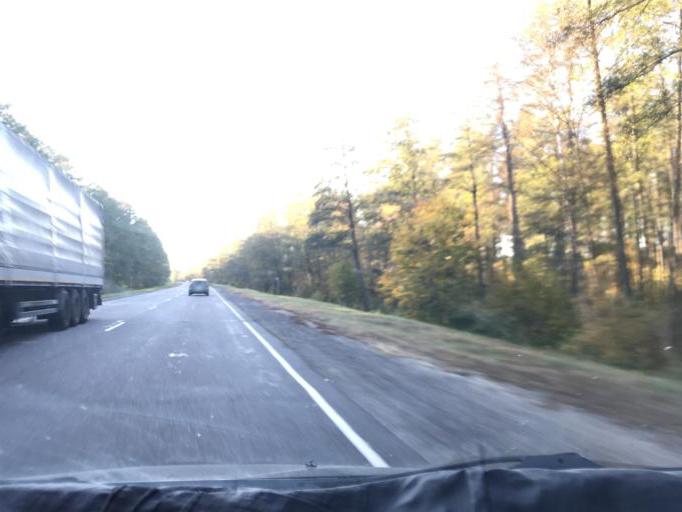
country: BY
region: Gomel
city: Pyetrykaw
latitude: 52.2735
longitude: 28.2582
